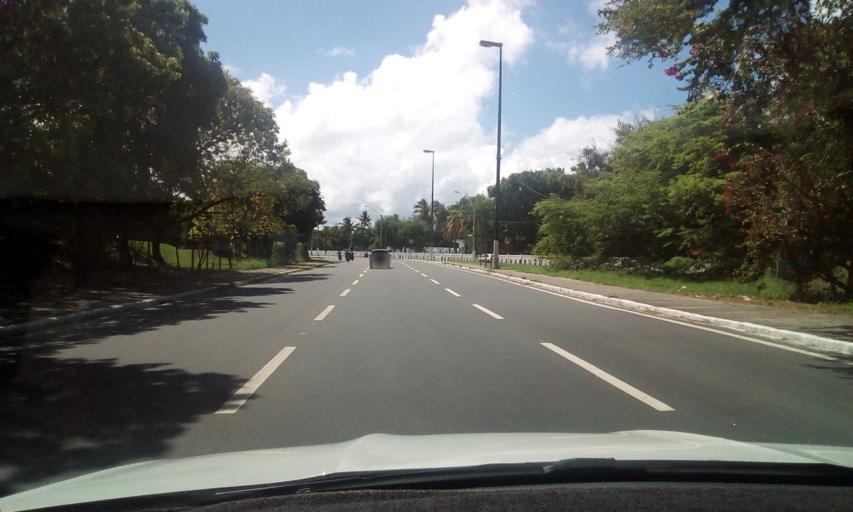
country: BR
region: Pernambuco
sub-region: Recife
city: Recife
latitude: -8.0351
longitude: -34.8687
